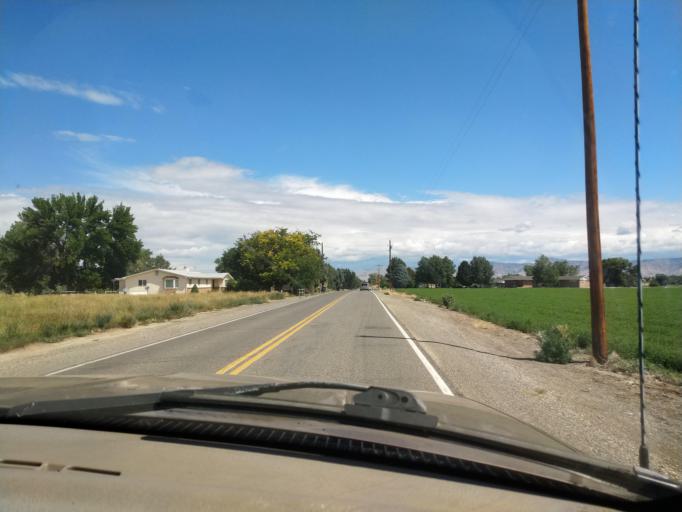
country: US
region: Colorado
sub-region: Mesa County
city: Redlands
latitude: 39.1327
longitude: -108.6080
